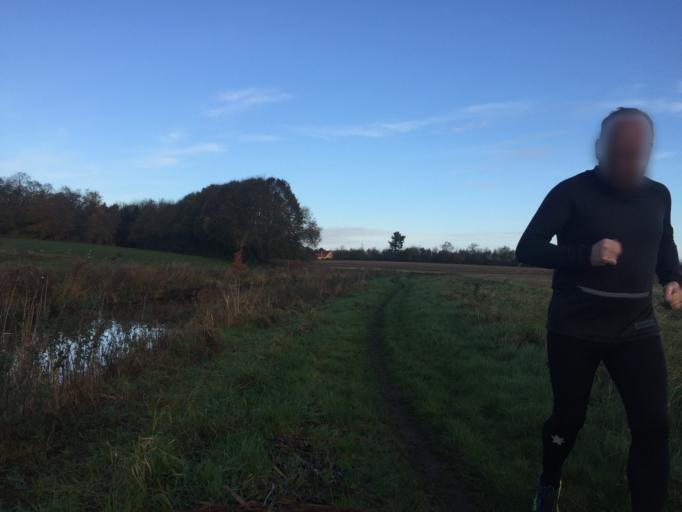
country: DK
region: Zealand
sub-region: Ringsted Kommune
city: Ringsted
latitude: 55.4632
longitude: 11.7582
